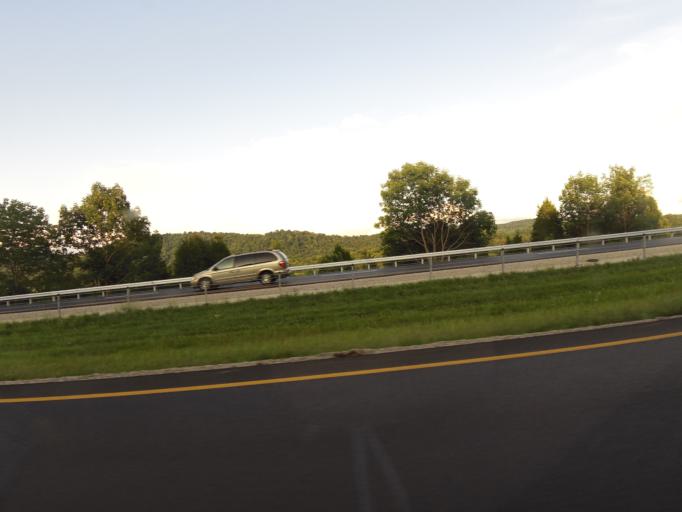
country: US
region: Kentucky
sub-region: Rockcastle County
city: Brodhead
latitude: 37.4543
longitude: -84.3359
